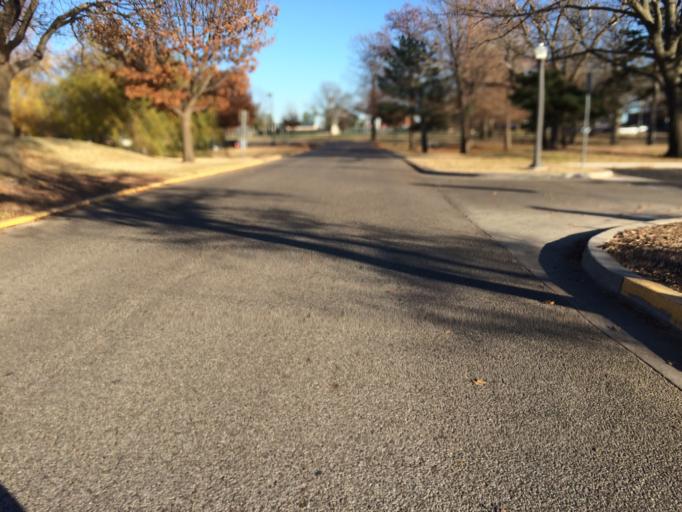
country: US
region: Oklahoma
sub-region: Cleveland County
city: Norman
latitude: 35.1951
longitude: -97.4461
